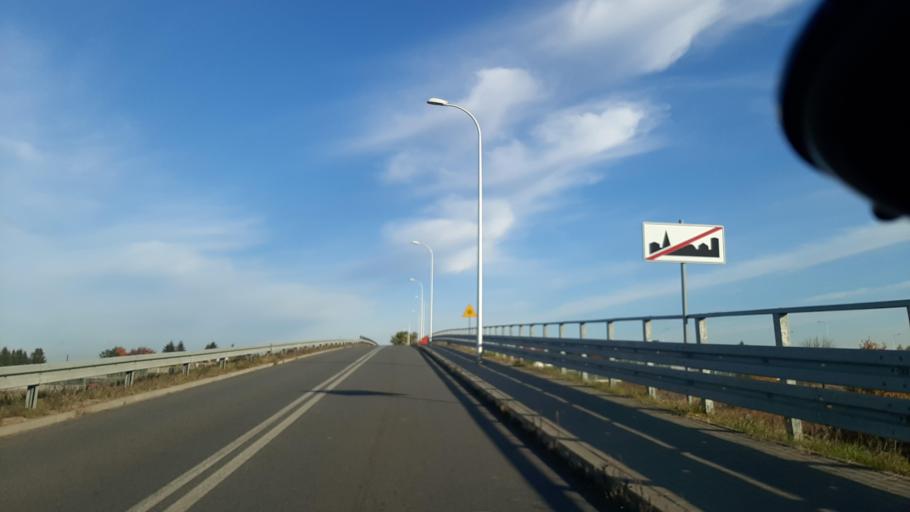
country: PL
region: Lublin Voivodeship
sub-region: Powiat lubelski
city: Lublin
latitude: 51.2995
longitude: 22.5629
